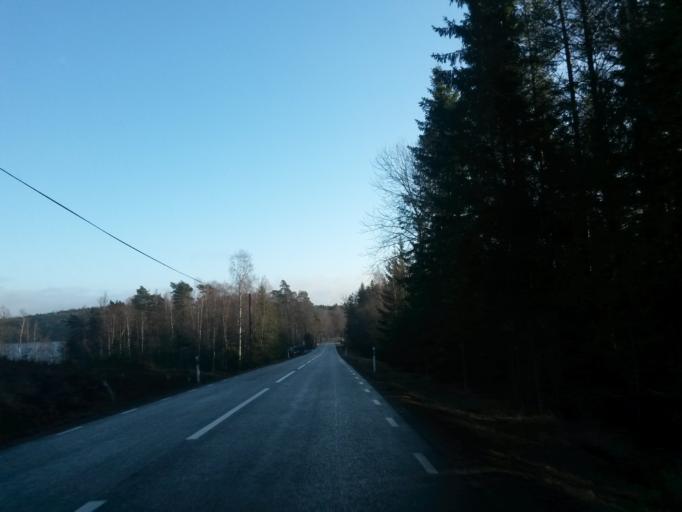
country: SE
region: Vaestra Goetaland
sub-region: Vargarda Kommun
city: Vargarda
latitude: 57.9149
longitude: 12.8911
